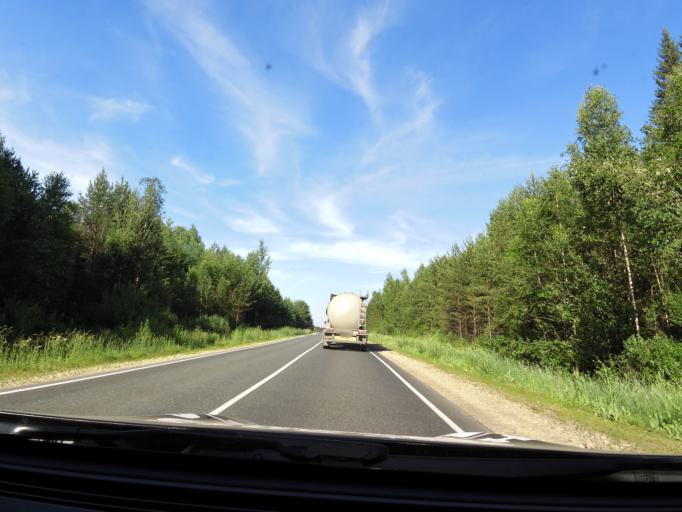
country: RU
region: Kirov
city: Belaya Kholunitsa
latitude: 58.8973
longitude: 50.9217
